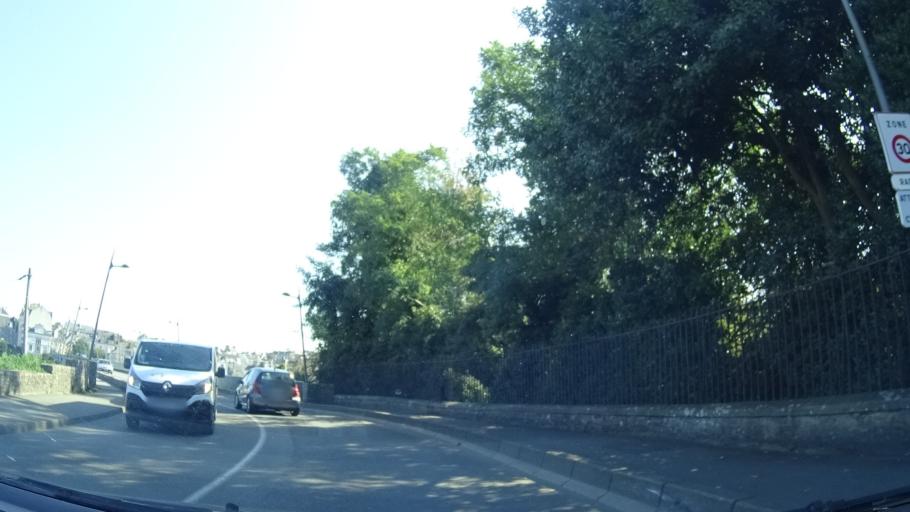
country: FR
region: Brittany
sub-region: Departement du Finistere
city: Douarnenez
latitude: 48.0896
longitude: -4.3348
